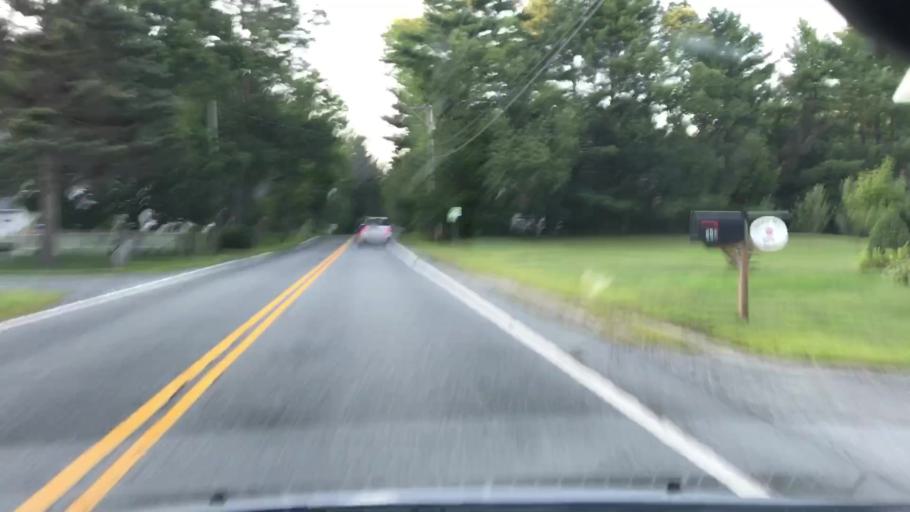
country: US
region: New Hampshire
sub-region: Grafton County
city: Rumney
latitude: 43.8746
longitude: -71.9126
